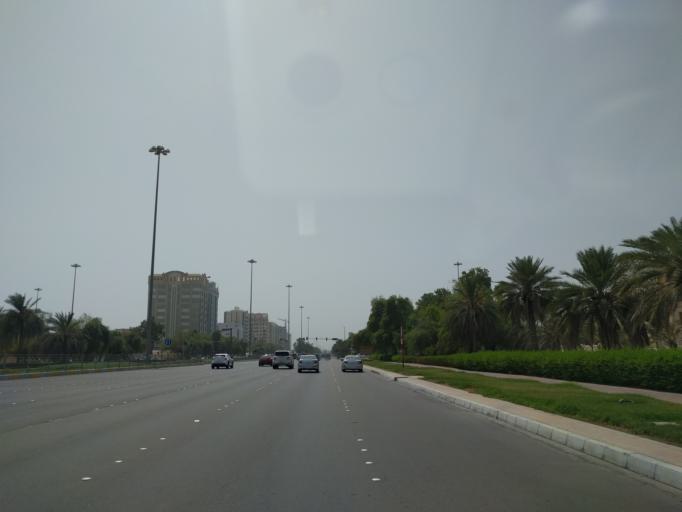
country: AE
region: Abu Dhabi
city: Abu Dhabi
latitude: 24.4372
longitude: 54.4181
